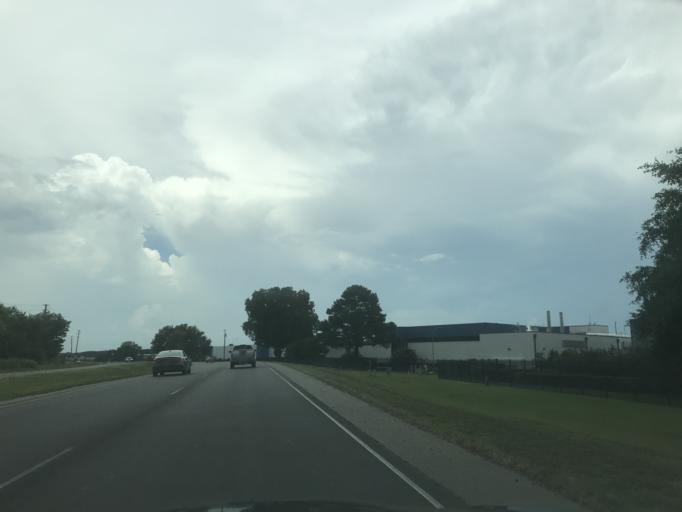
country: US
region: North Carolina
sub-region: Johnston County
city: Clayton
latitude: 35.6201
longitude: -78.4209
